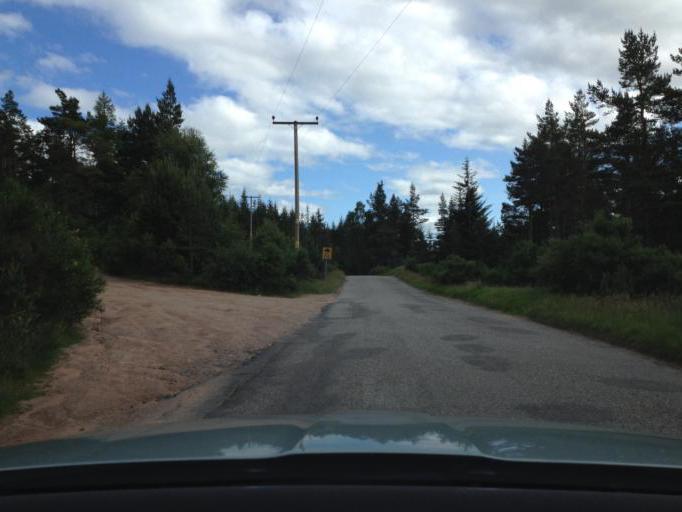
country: GB
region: Scotland
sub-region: Aberdeenshire
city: Banchory
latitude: 56.9886
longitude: -2.5762
